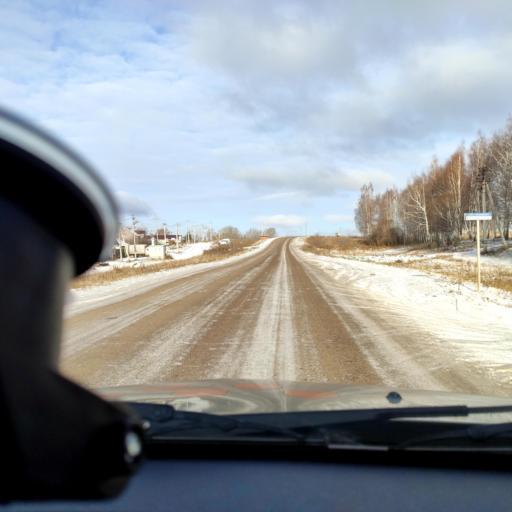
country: RU
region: Bashkortostan
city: Mikhaylovka
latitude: 54.8012
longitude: 55.7795
